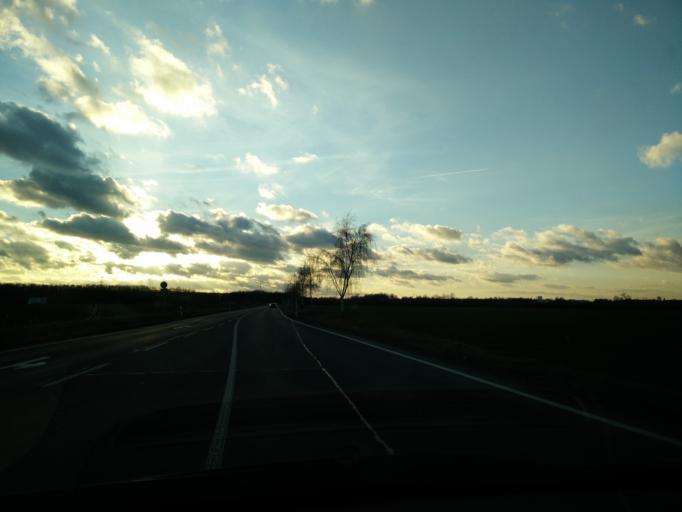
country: DE
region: Saxony
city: Bohlen
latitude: 51.2179
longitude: 12.3654
